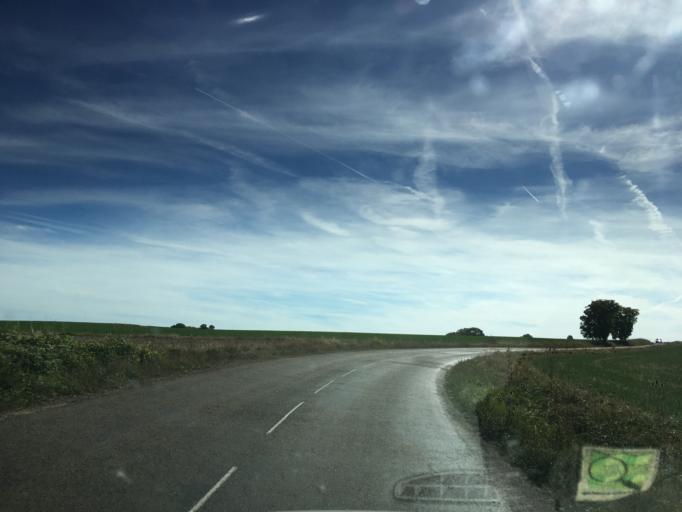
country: FR
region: Bourgogne
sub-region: Departement de l'Yonne
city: Vermenton
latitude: 47.5910
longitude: 3.6998
